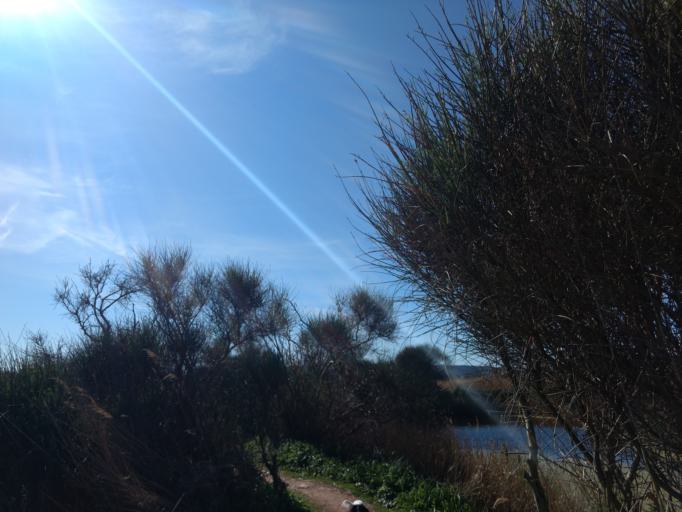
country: FR
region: Languedoc-Roussillon
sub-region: Departement de l'Herault
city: Mireval
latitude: 43.5129
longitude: 3.8311
